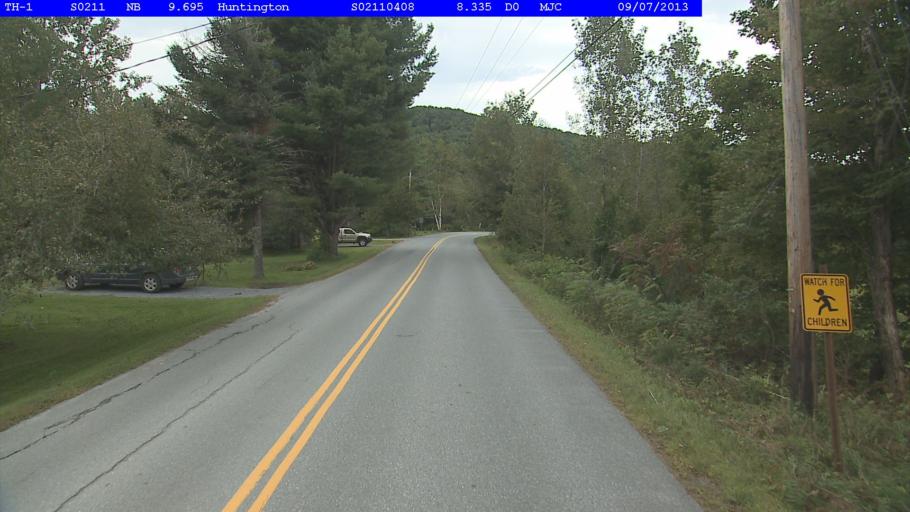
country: US
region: Vermont
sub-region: Chittenden County
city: Hinesburg
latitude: 44.3357
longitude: -72.9962
